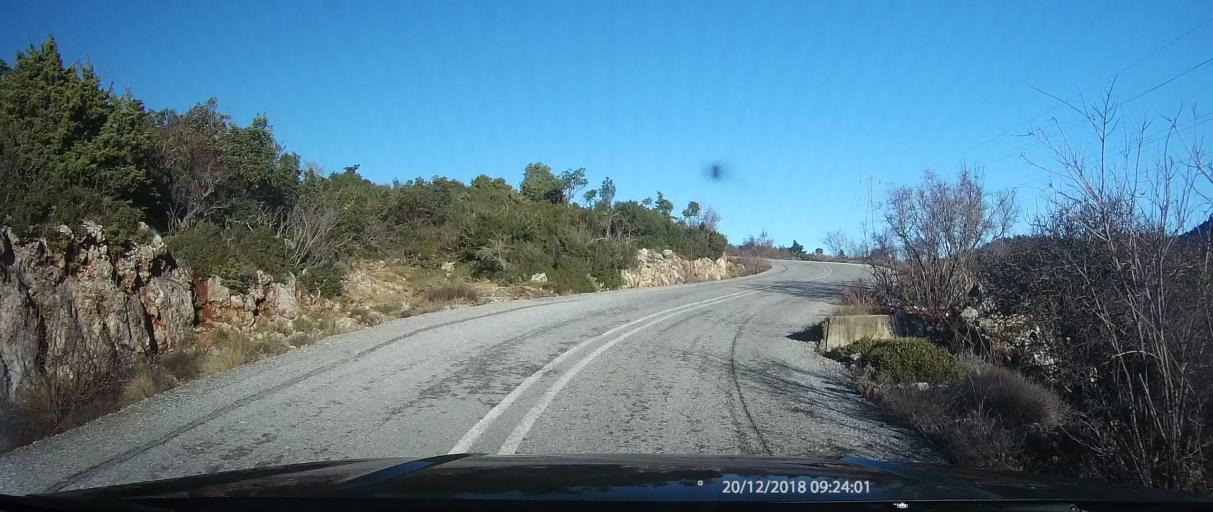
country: GR
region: Peloponnese
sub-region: Nomos Lakonias
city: Molaoi
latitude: 36.9617
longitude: 22.8928
